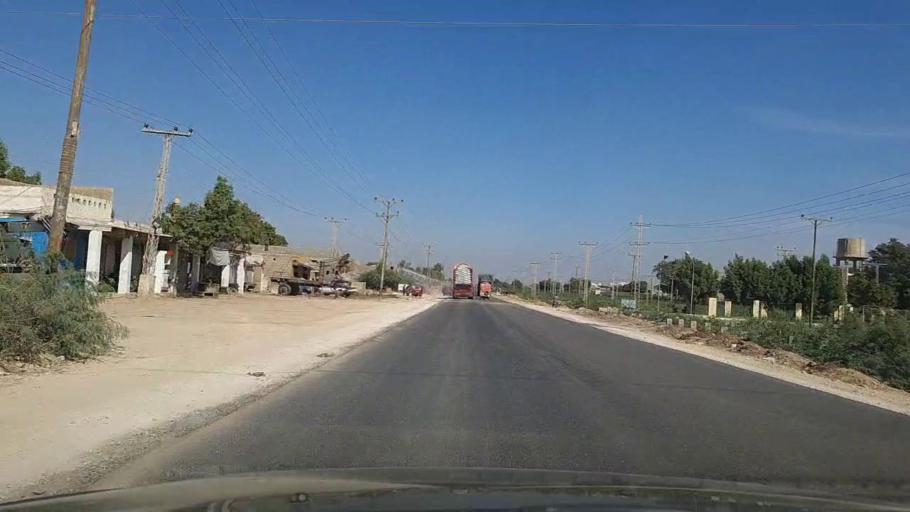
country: PK
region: Sindh
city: Kotri
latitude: 25.3430
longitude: 68.2558
